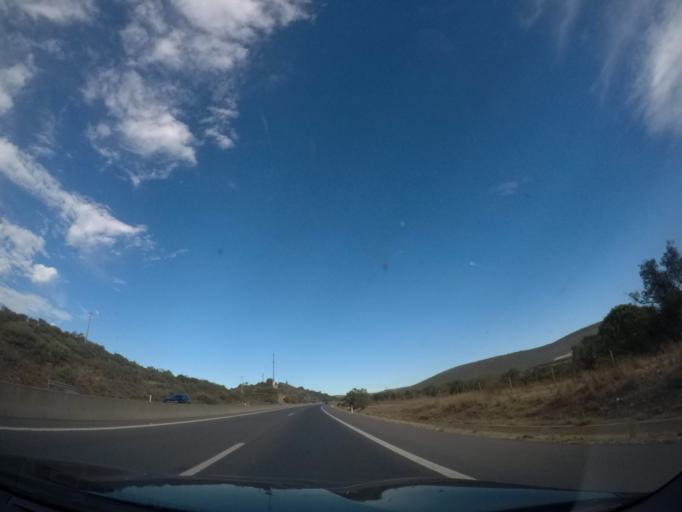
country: PT
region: Faro
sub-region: Loule
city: Vilamoura
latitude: 37.1306
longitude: -8.1013
